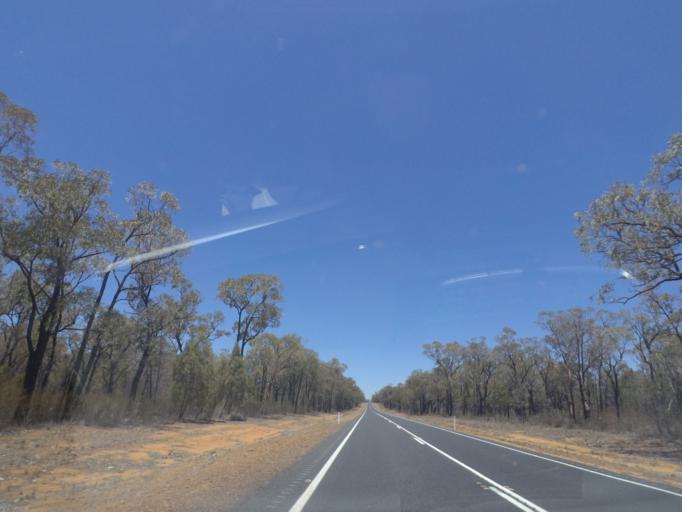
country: AU
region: New South Wales
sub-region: Narrabri
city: Narrabri
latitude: -30.7373
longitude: 149.5173
